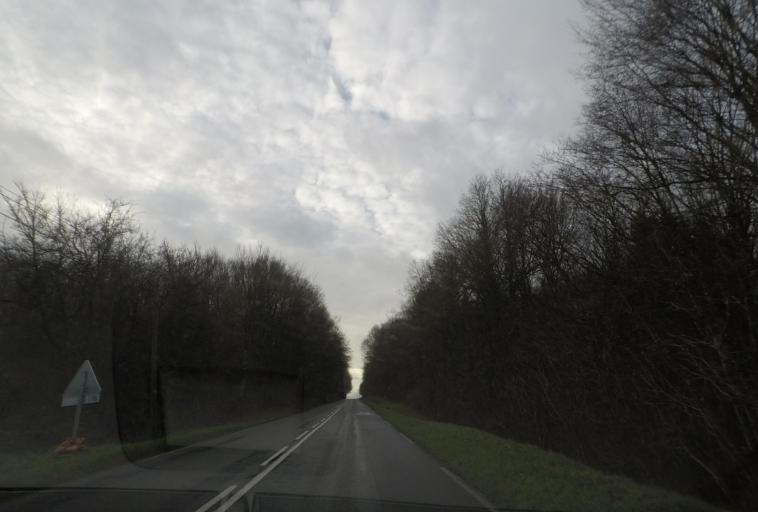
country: FR
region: Pays de la Loire
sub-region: Departement de la Sarthe
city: Saint-Calais
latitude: 47.9595
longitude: 0.7558
